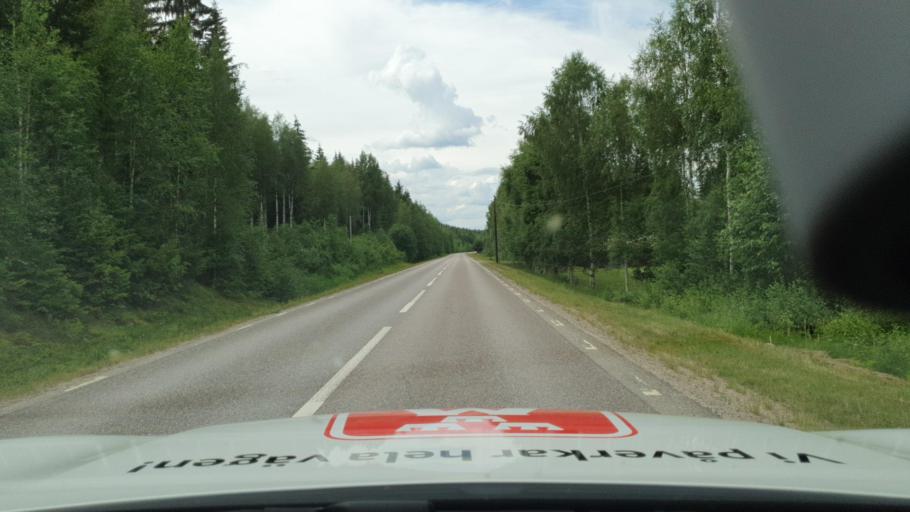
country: NO
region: Hedmark
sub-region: Trysil
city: Innbygda
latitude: 60.9014
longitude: 12.5746
